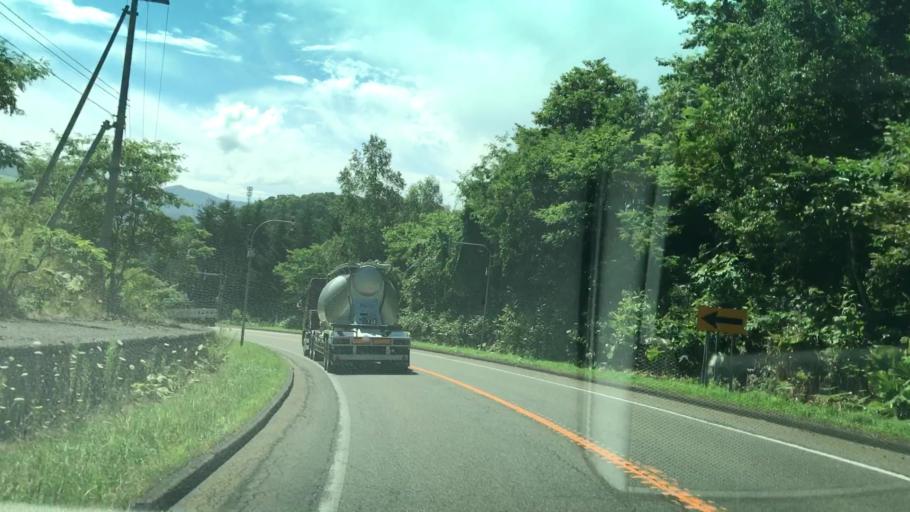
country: JP
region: Hokkaido
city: Shimo-furano
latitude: 42.8912
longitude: 142.4350
